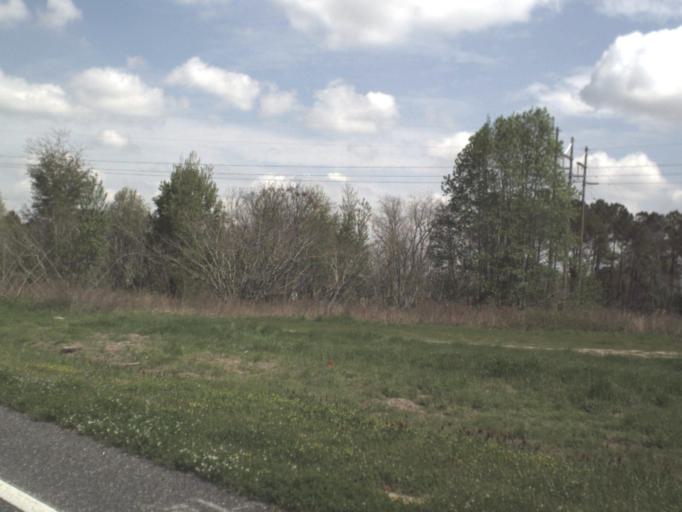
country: US
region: Florida
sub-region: Gadsden County
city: Havana
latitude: 30.6888
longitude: -84.3804
